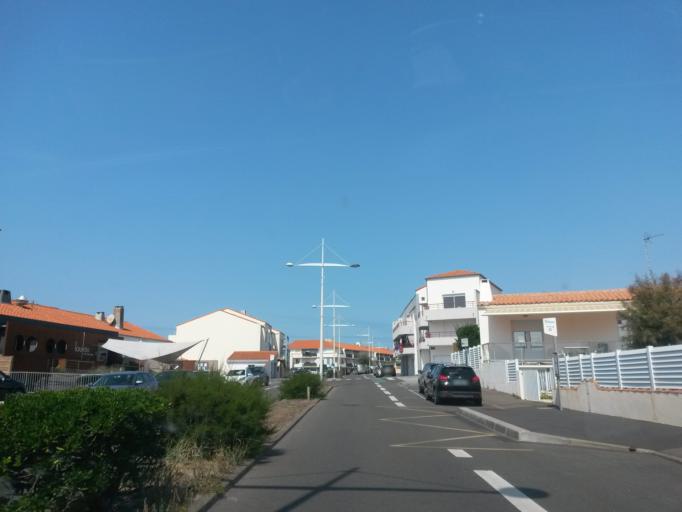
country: FR
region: Pays de la Loire
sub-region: Departement de la Vendee
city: Les Sables-d'Olonne
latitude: 46.4933
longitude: -1.8104
